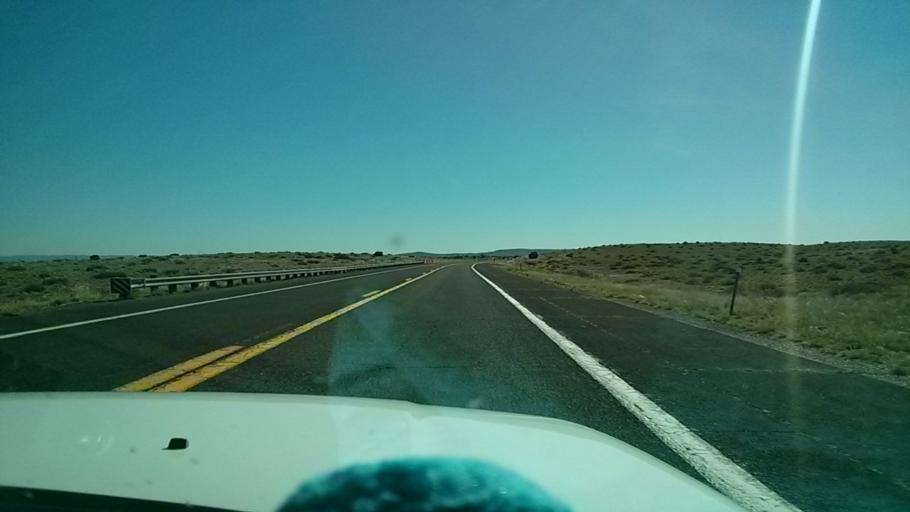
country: US
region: Arizona
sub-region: Mohave County
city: Peach Springs
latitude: 35.5207
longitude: -113.4892
